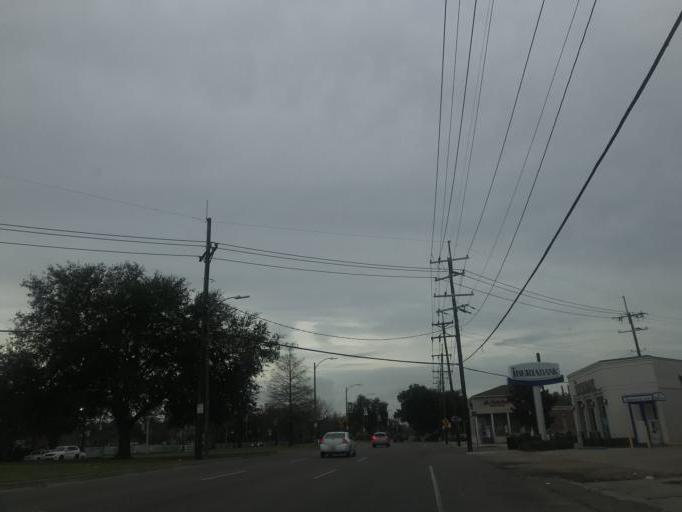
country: US
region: Louisiana
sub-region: Orleans Parish
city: New Orleans
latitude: 29.9459
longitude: -90.1136
